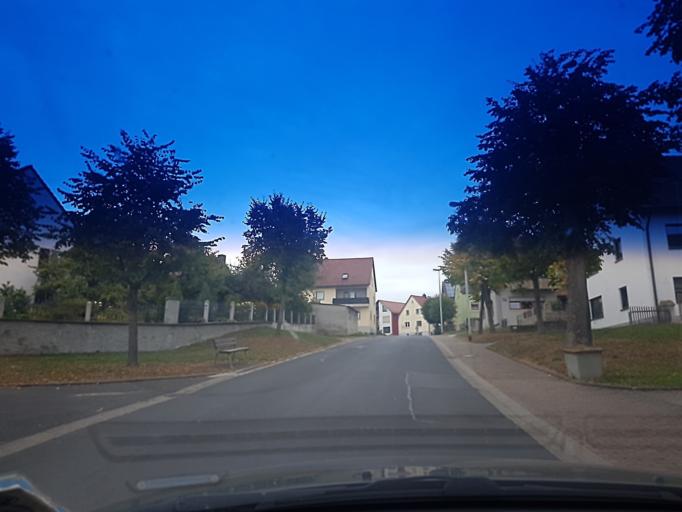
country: DE
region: Bavaria
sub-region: Regierungsbezirk Unterfranken
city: Geiselwind
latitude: 49.8323
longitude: 10.4820
